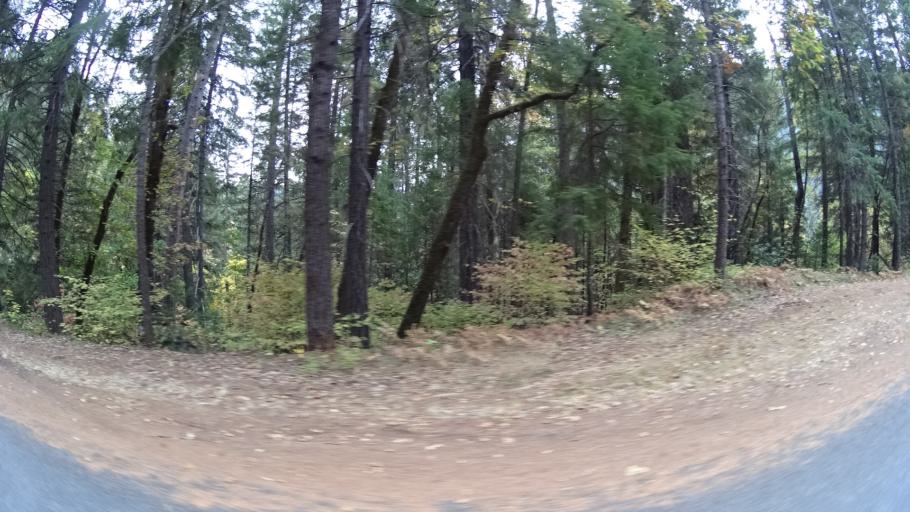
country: US
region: California
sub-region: Siskiyou County
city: Happy Camp
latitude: 41.7742
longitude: -123.3783
